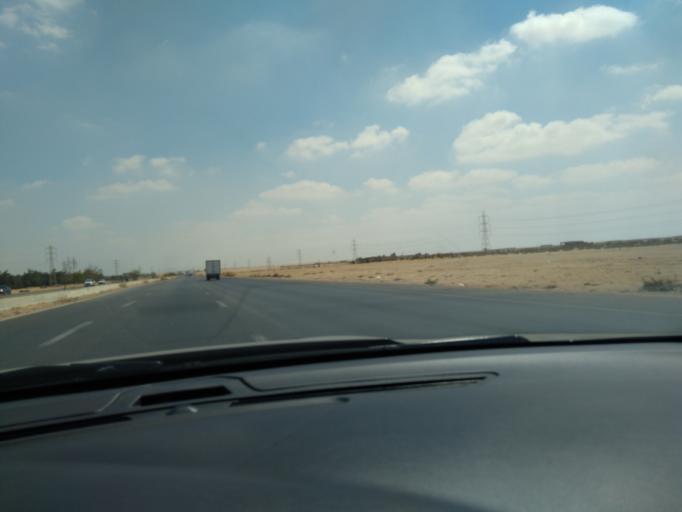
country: EG
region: Al Isma'iliyah
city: At Tall al Kabir
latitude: 30.3560
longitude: 31.8959
